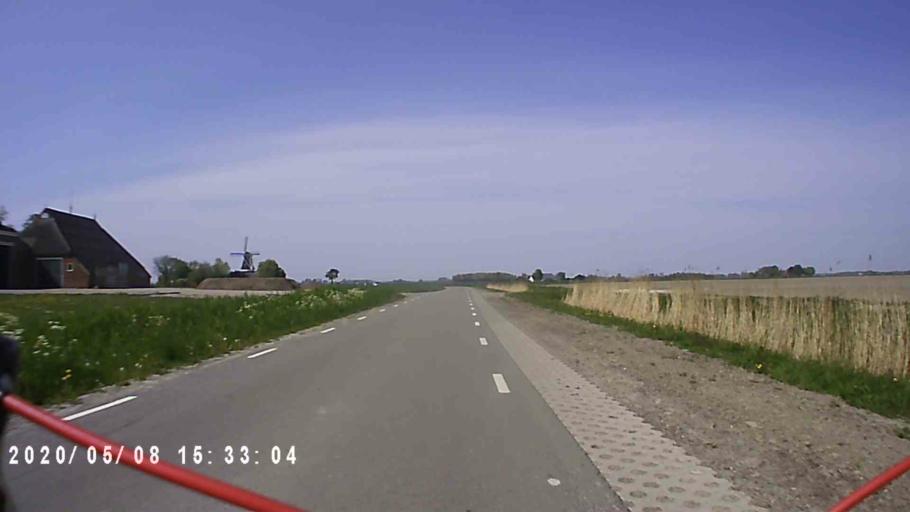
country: NL
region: Groningen
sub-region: Gemeente Appingedam
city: Appingedam
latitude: 53.3672
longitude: 6.7261
